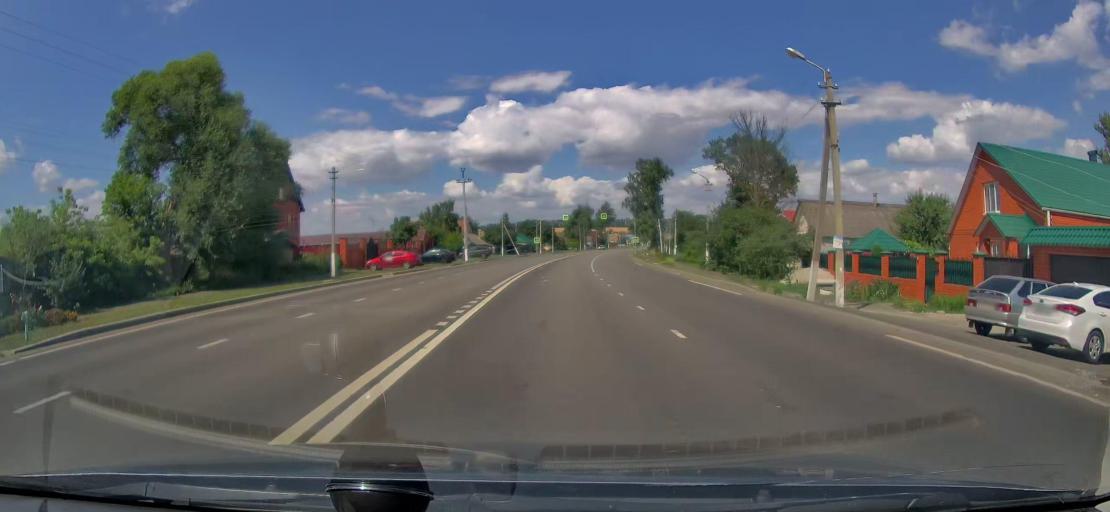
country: RU
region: Kursk
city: Zolotukhino
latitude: 51.9457
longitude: 36.3049
